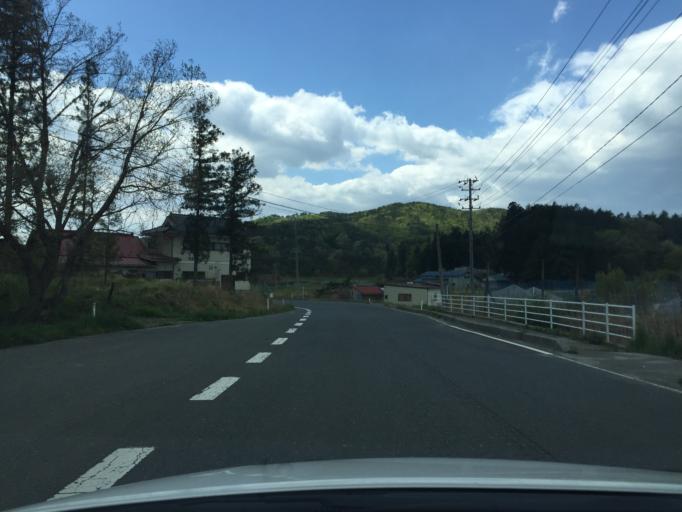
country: JP
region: Fukushima
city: Yanagawamachi-saiwaicho
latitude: 37.7073
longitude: 140.6953
